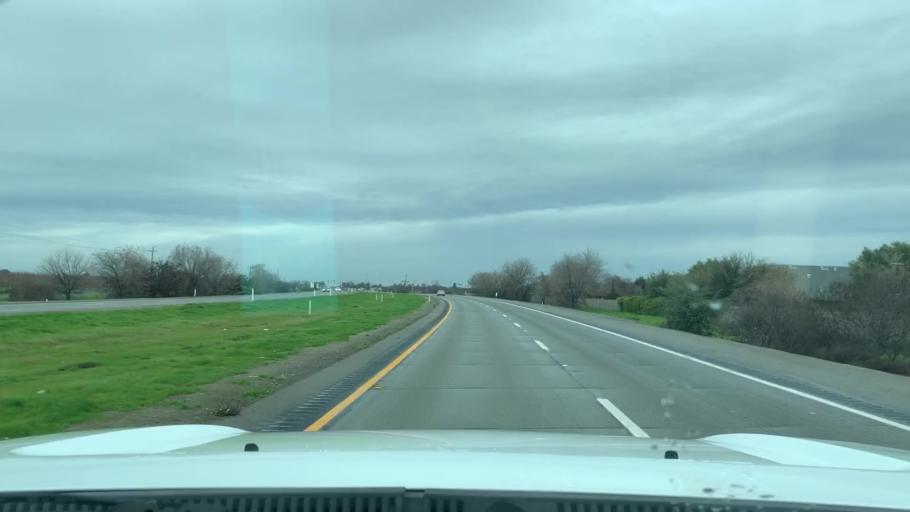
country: US
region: California
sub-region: Kings County
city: Lemoore
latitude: 36.3076
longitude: -119.8081
